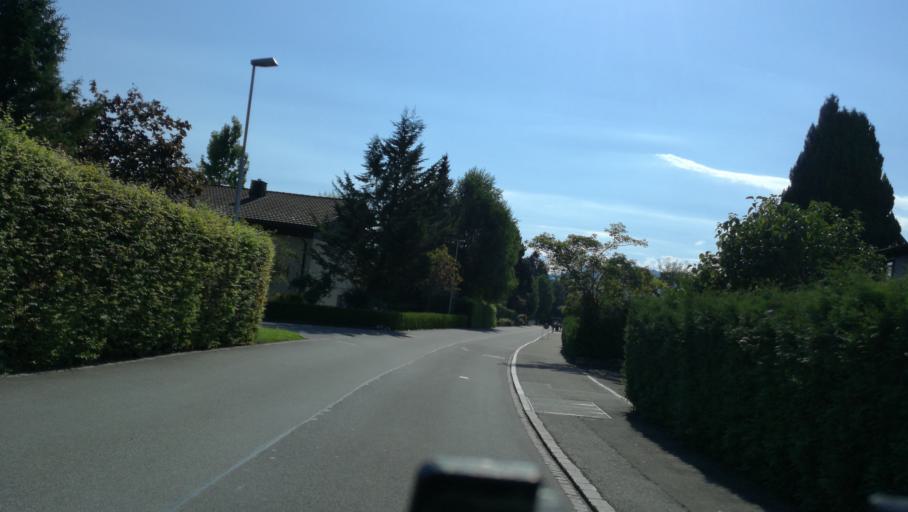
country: CH
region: Zug
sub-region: Zug
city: Unterageri
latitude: 47.1351
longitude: 8.5885
